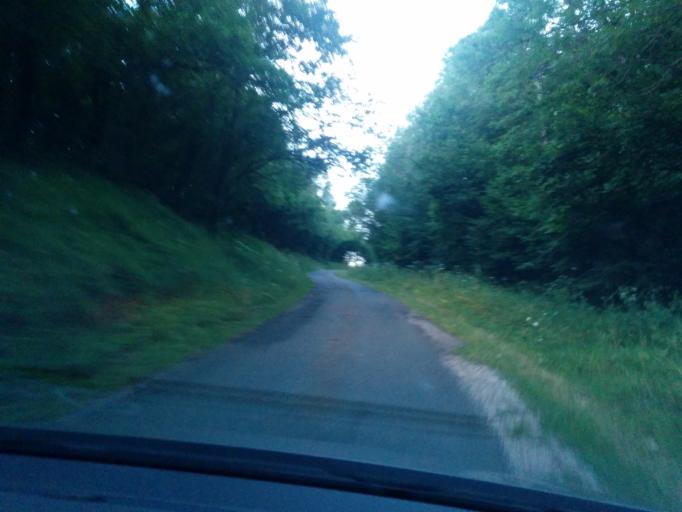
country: FR
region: Franche-Comte
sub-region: Departement du Jura
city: Valfin-les-Saint-Claude
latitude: 46.4419
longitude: 5.8217
